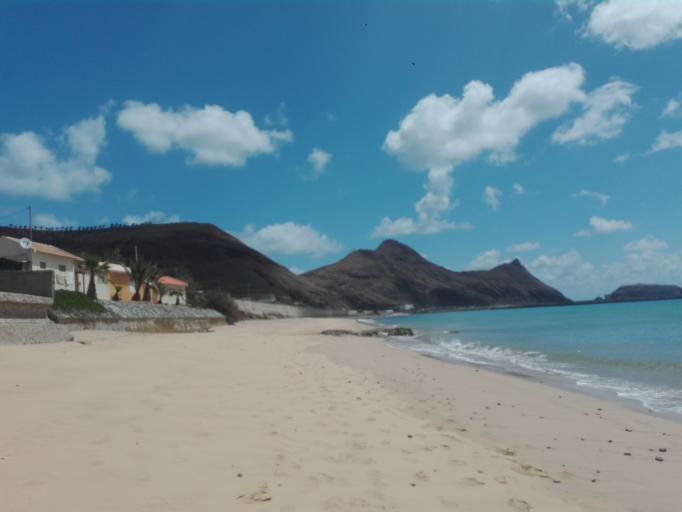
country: PT
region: Madeira
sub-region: Porto Santo
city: Vila de Porto Santo
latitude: 33.0618
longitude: -16.3256
